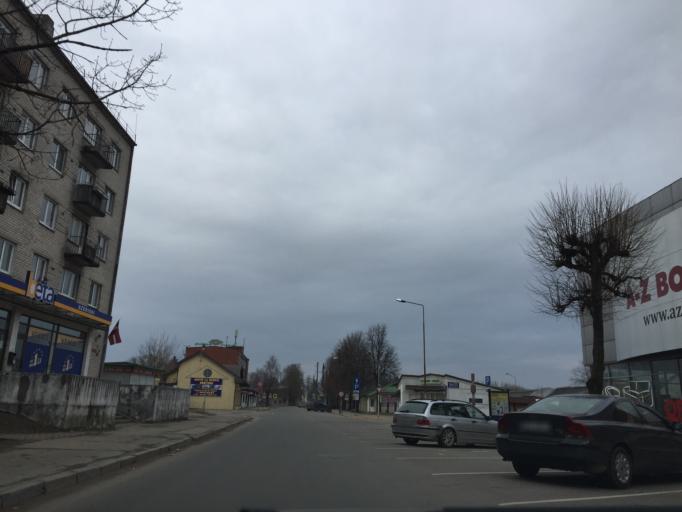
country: LV
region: Jelgava
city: Jelgava
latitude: 56.6559
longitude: 23.7222
